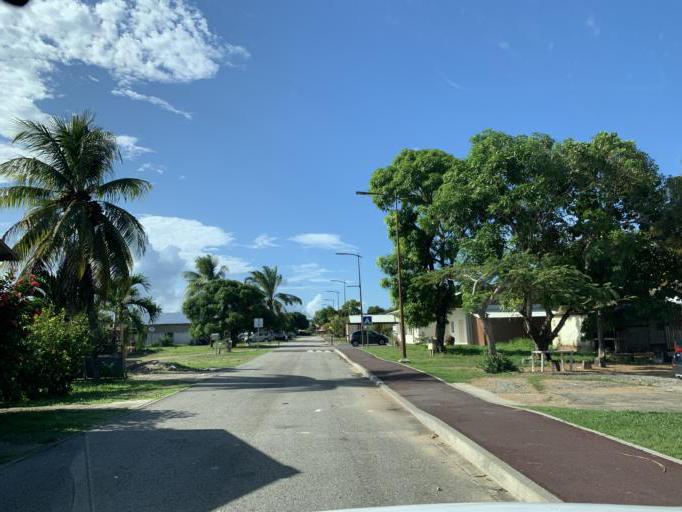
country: GF
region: Guyane
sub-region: Guyane
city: Kourou
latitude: 5.1726
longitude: -52.6444
